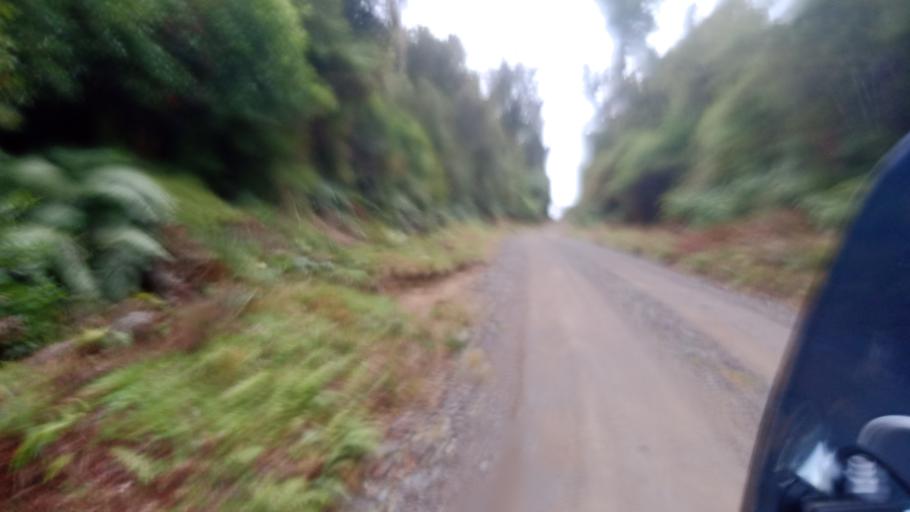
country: NZ
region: Bay of Plenty
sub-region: Whakatane District
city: Murupara
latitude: -38.6860
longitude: 176.6094
